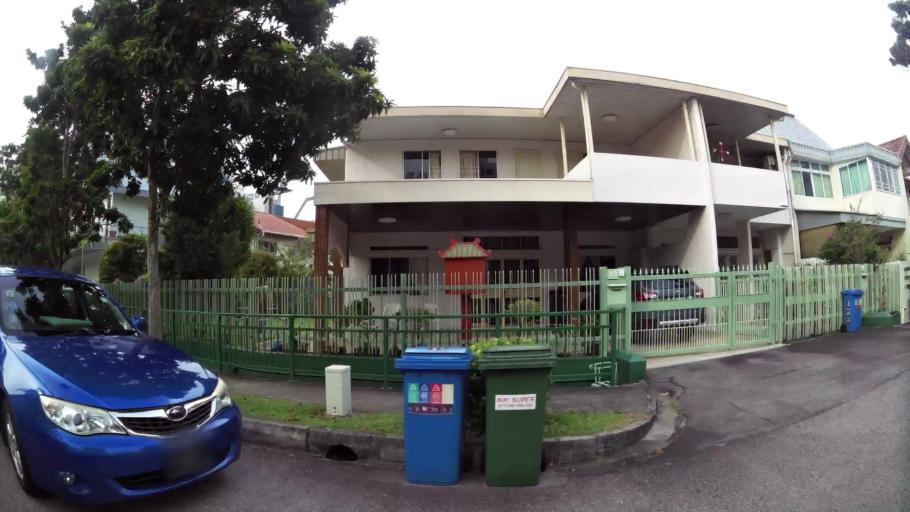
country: SG
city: Singapore
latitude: 1.3496
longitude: 103.8435
